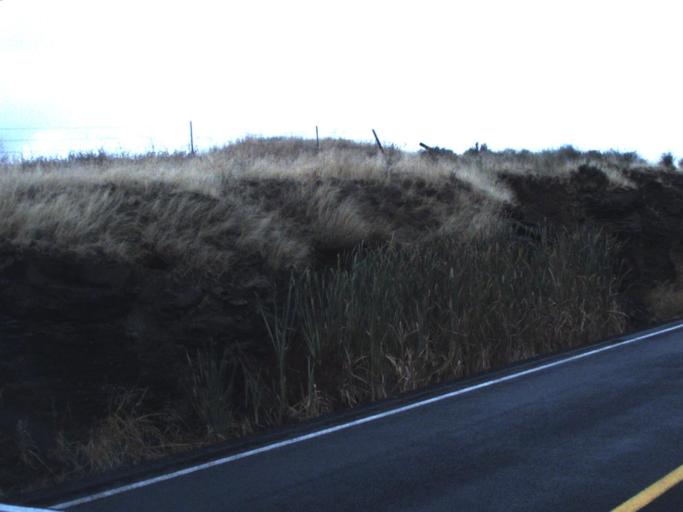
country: US
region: Washington
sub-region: Spokane County
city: Cheney
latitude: 47.1245
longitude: -117.7621
